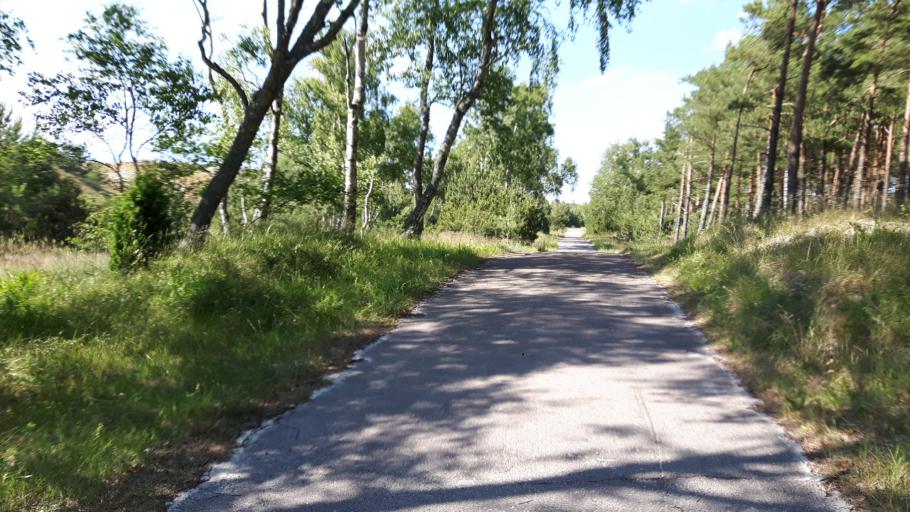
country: LT
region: Klaipedos apskritis
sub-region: Klaipeda
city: Klaipeda
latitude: 55.6896
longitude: 21.1033
